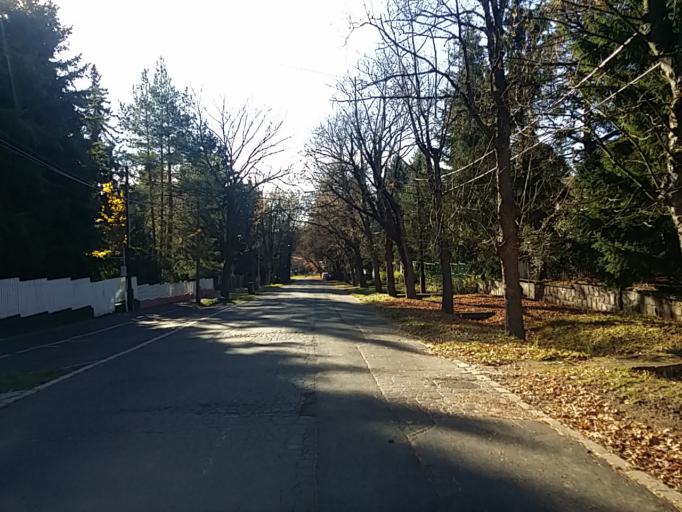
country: HU
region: Heves
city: Gyongyossolymos
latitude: 47.8324
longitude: 19.9648
